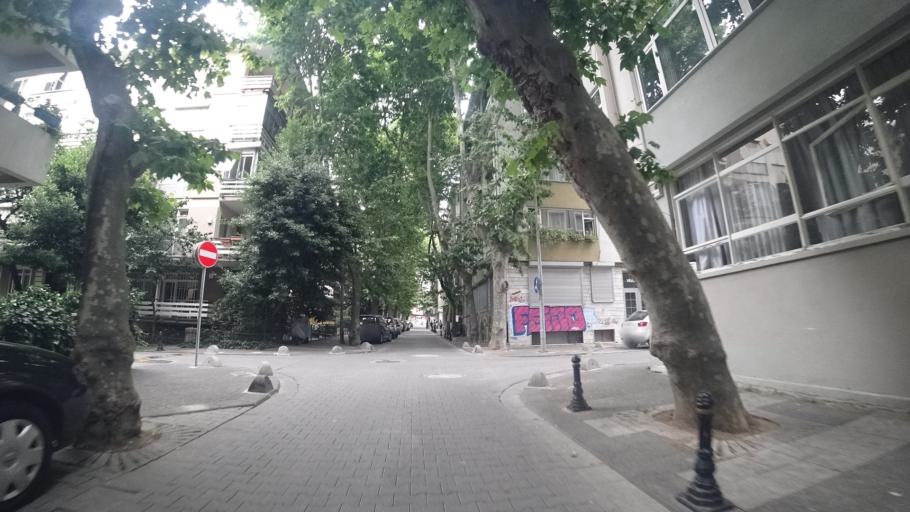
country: TR
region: Istanbul
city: UEskuedar
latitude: 40.9806
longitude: 29.0222
